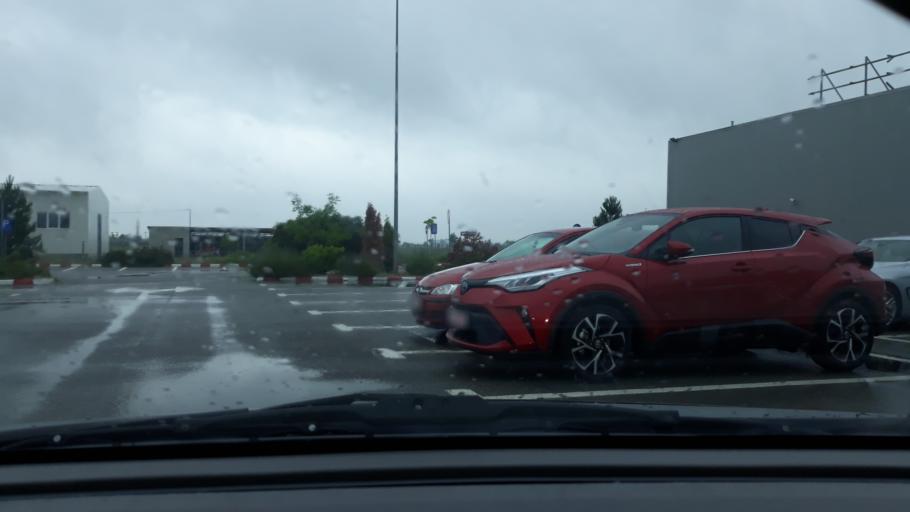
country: RO
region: Bihor
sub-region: Comuna Biharea
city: Biharea
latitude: 47.1113
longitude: 21.8928
